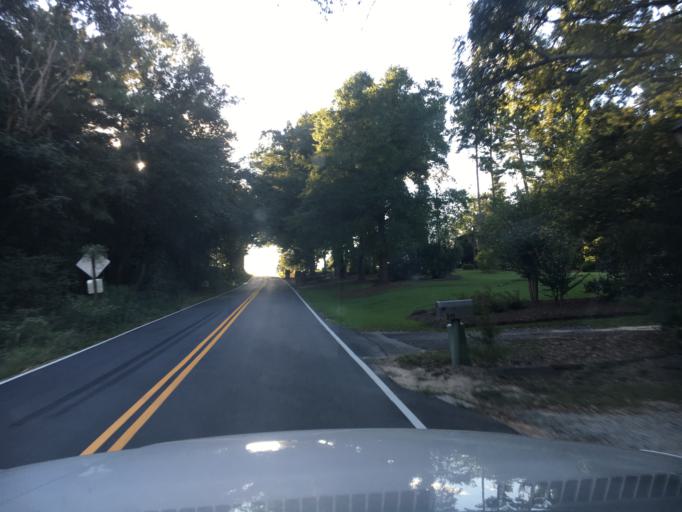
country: US
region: South Carolina
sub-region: Spartanburg County
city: Roebuck
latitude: 34.9010
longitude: -82.0002
